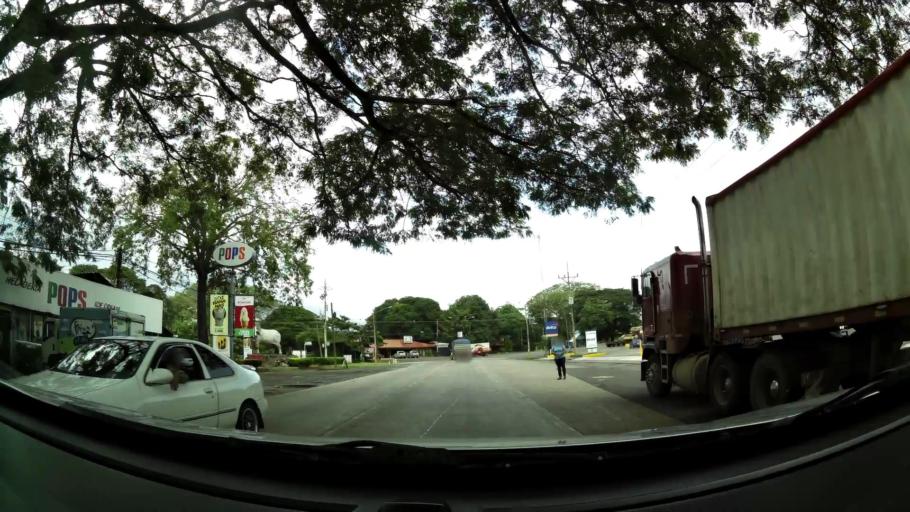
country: CR
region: Guanacaste
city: Juntas
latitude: 10.2654
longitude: -85.0217
